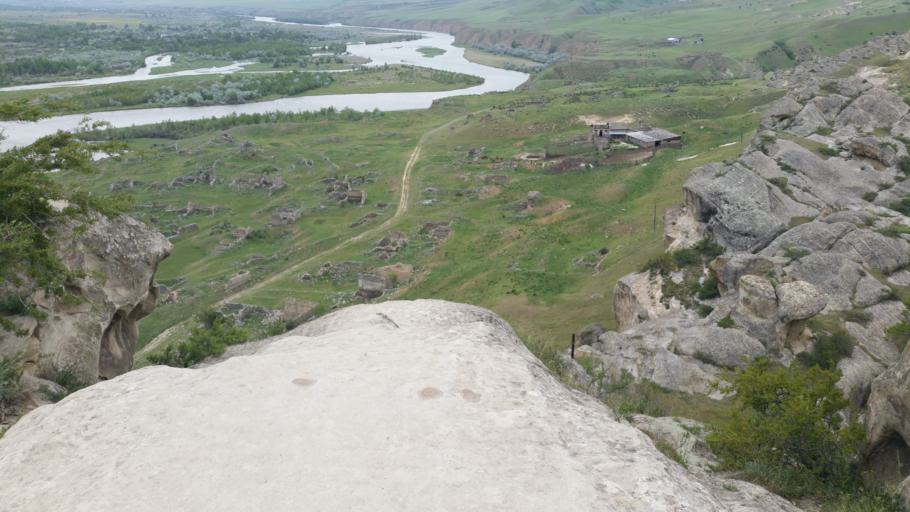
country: GE
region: Shida Kartli
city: Gori
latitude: 41.9677
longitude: 44.2067
